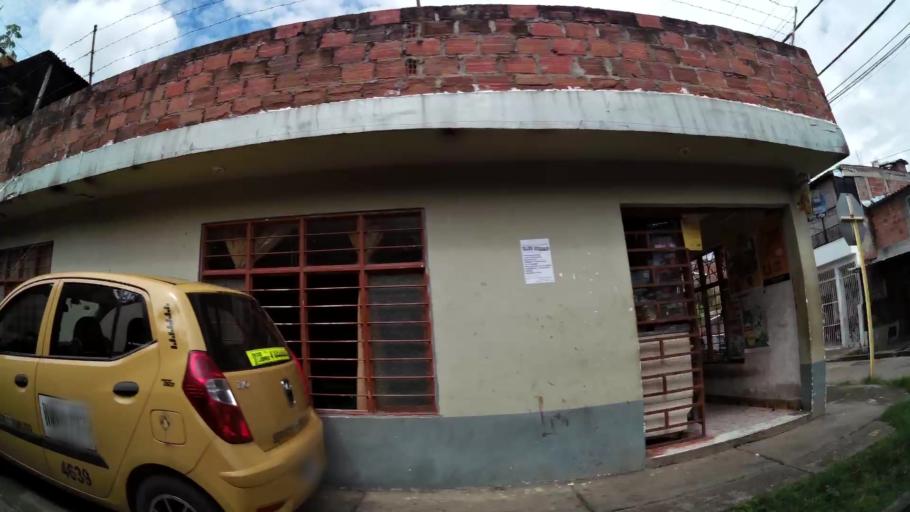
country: CO
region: Valle del Cauca
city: Cali
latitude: 3.3882
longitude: -76.5550
